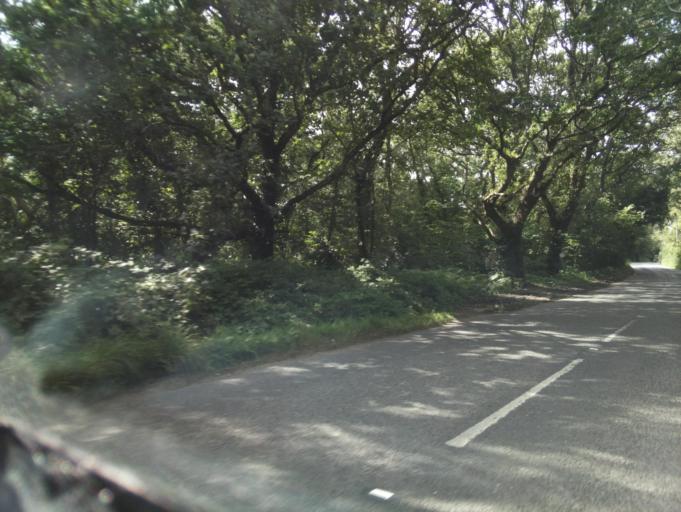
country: GB
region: England
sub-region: Hampshire
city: New Milton
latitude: 50.7412
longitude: -1.6447
